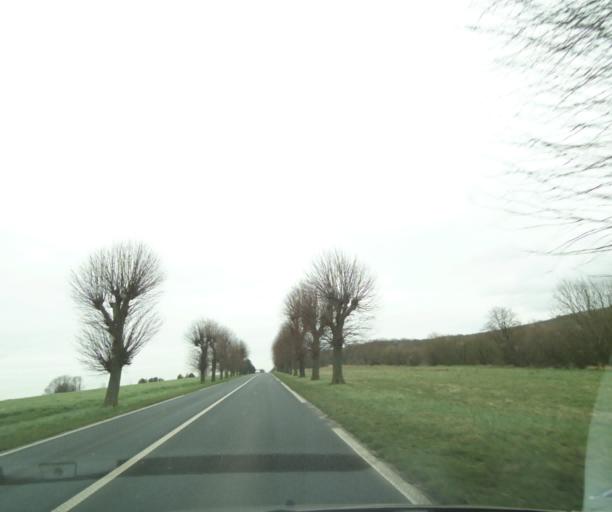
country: FR
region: Picardie
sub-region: Departement de l'Oise
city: Crisolles
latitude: 49.6062
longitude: 3.0160
